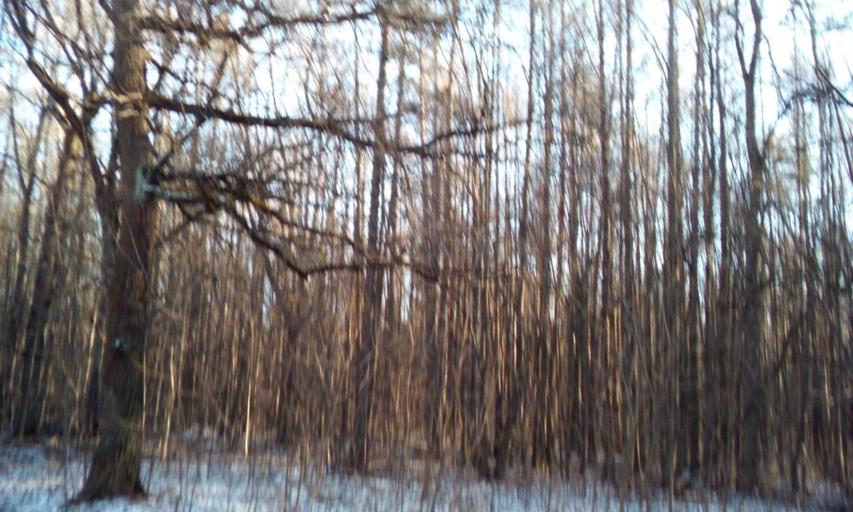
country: RU
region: Moskovskaya
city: Aprelevka
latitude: 55.5544
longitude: 37.0939
